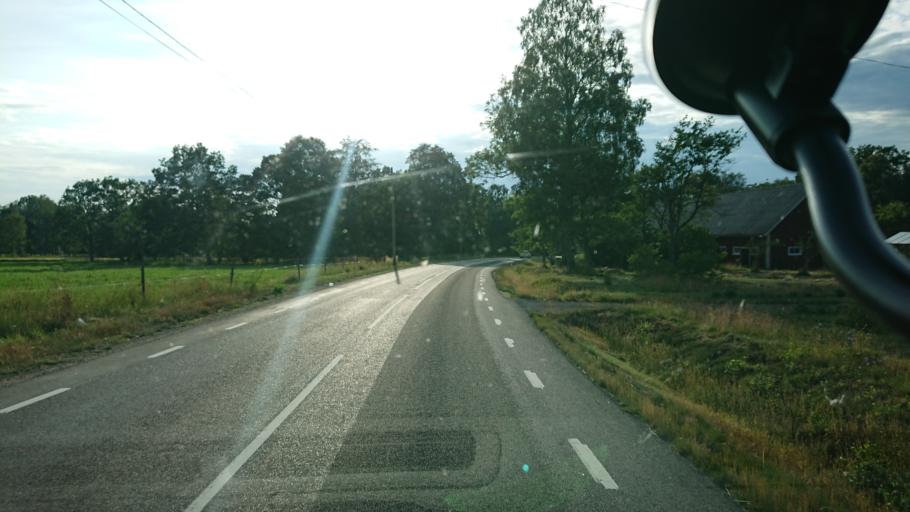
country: SE
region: Kronoberg
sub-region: Vaxjo Kommun
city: Braas
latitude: 57.0211
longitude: 15.0361
